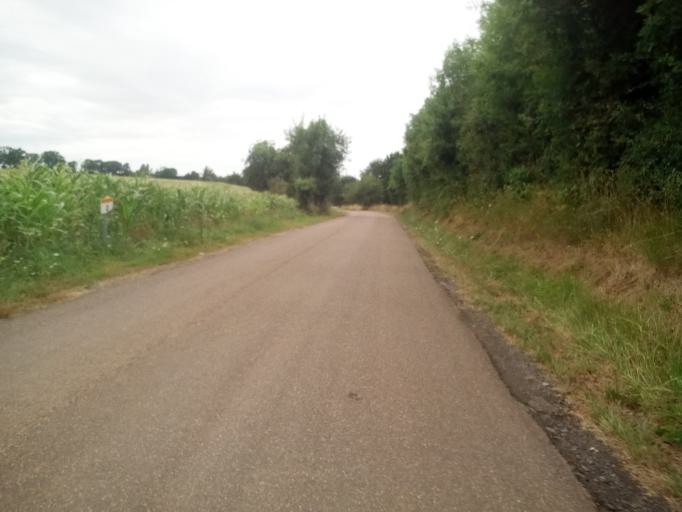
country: FR
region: Lower Normandy
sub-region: Departement du Calvados
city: Clinchamps-sur-Orne
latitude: 49.0350
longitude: -0.3938
